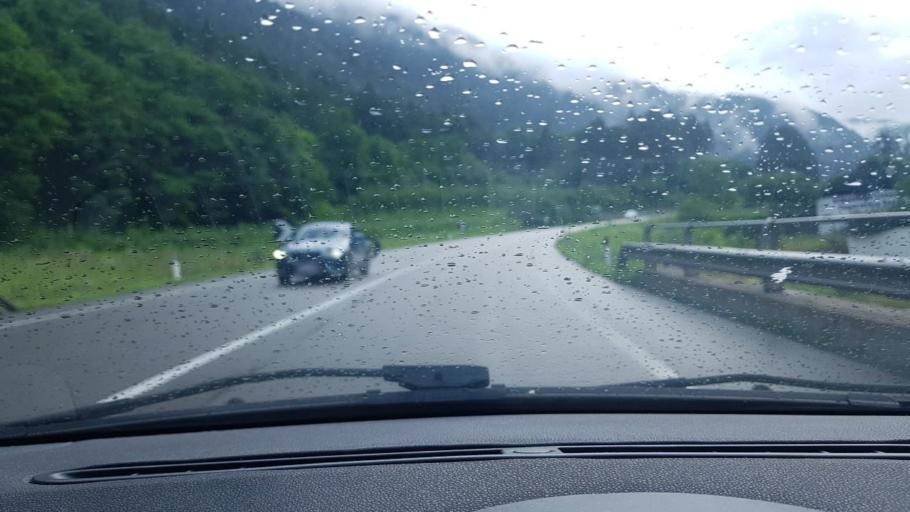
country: IT
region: Trentino-Alto Adige
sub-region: Bolzano
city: Rodengo
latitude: 46.8124
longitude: 11.6845
